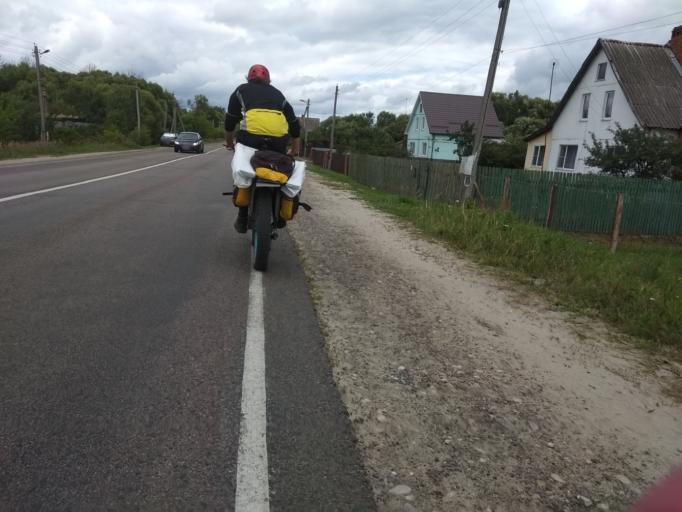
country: RU
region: Moskovskaya
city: Misheronskiy
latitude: 55.6001
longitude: 39.7056
